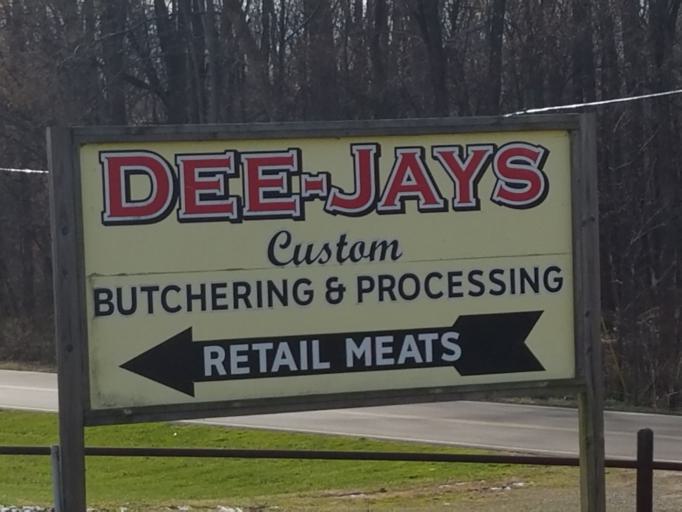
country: US
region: Ohio
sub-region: Knox County
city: Fredericktown
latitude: 40.4931
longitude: -82.5433
